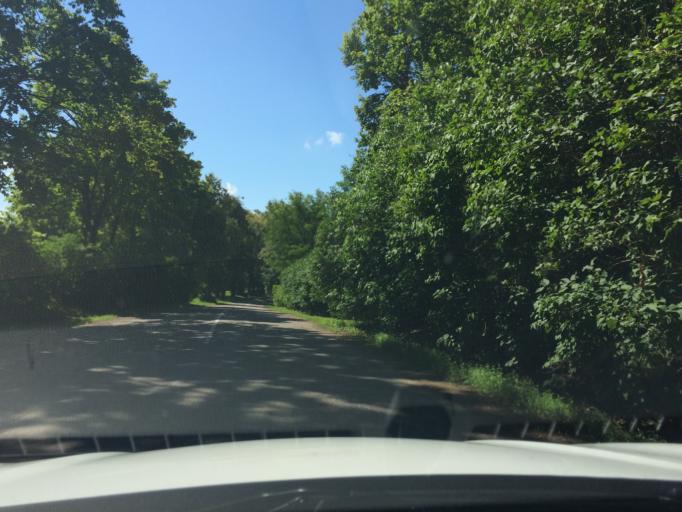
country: LV
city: Tervete
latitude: 56.5293
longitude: 23.5105
